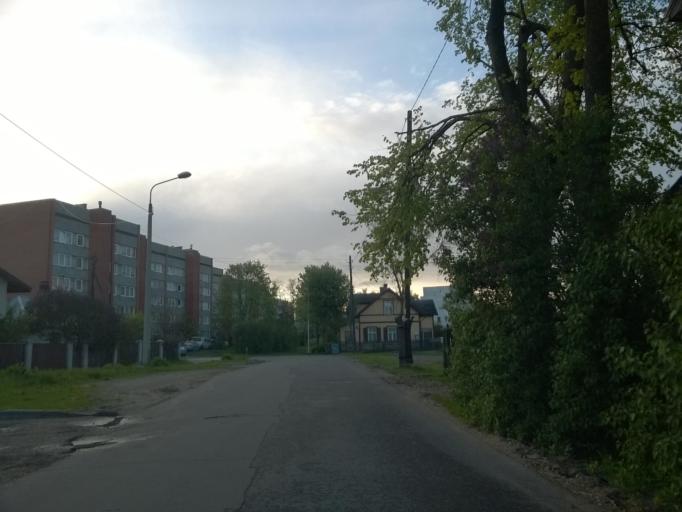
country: LV
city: Tireli
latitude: 56.9486
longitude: 23.6193
